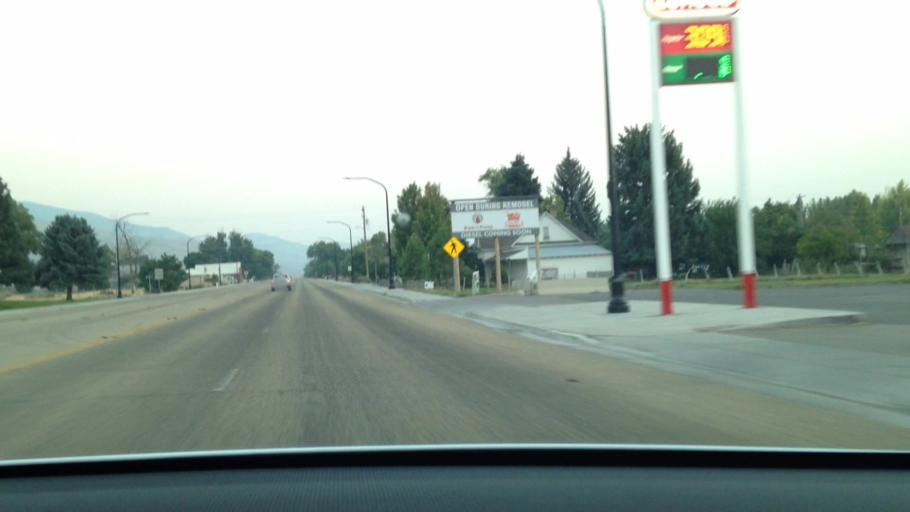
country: US
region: Utah
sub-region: Juab County
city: Nephi
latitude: 39.5586
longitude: -111.8639
